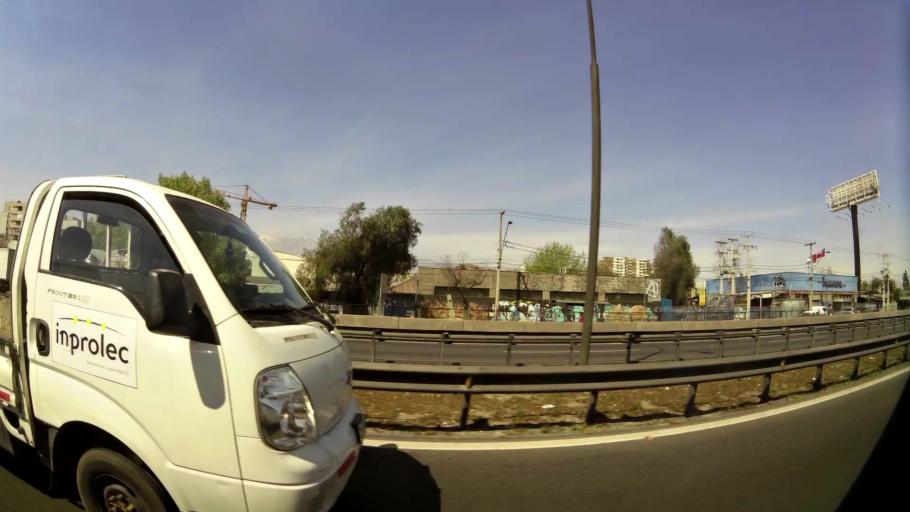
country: CL
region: Santiago Metropolitan
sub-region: Provincia de Santiago
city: Santiago
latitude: -33.4831
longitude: -70.6581
